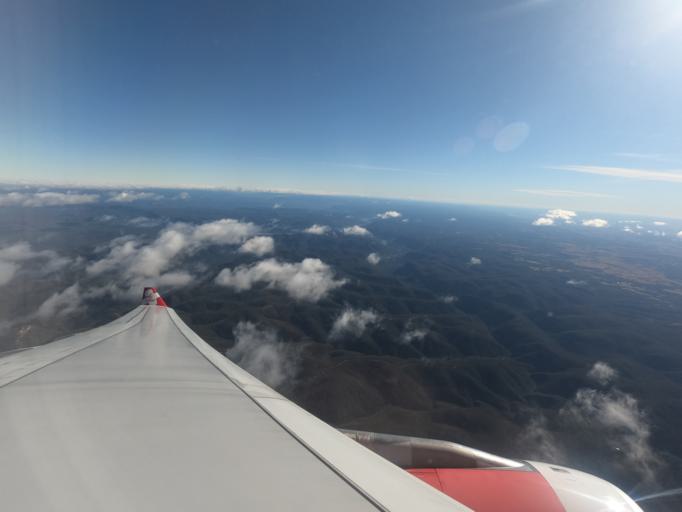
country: AU
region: New South Wales
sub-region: Wollondilly
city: Buxton
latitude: -34.2695
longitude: 150.4480
